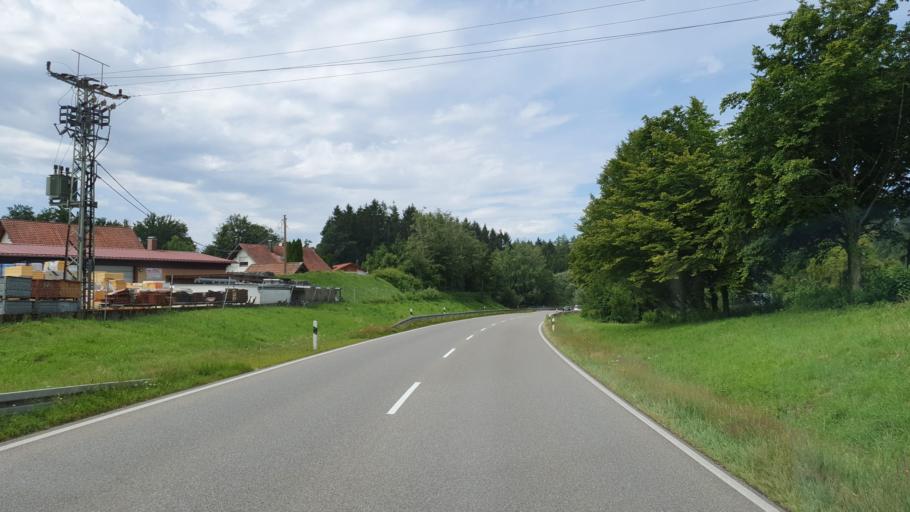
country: DE
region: Bavaria
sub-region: Swabia
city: Weissensberg
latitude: 47.5749
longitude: 9.7263
